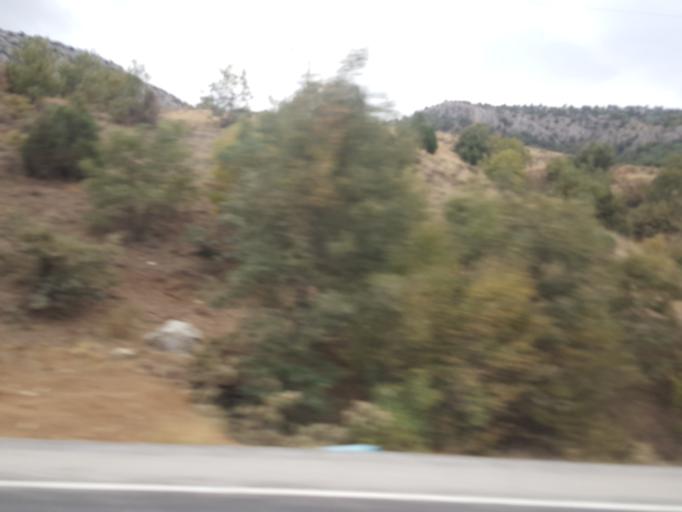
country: TR
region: Yozgat
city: Cekerek
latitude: 40.2067
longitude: 35.4742
